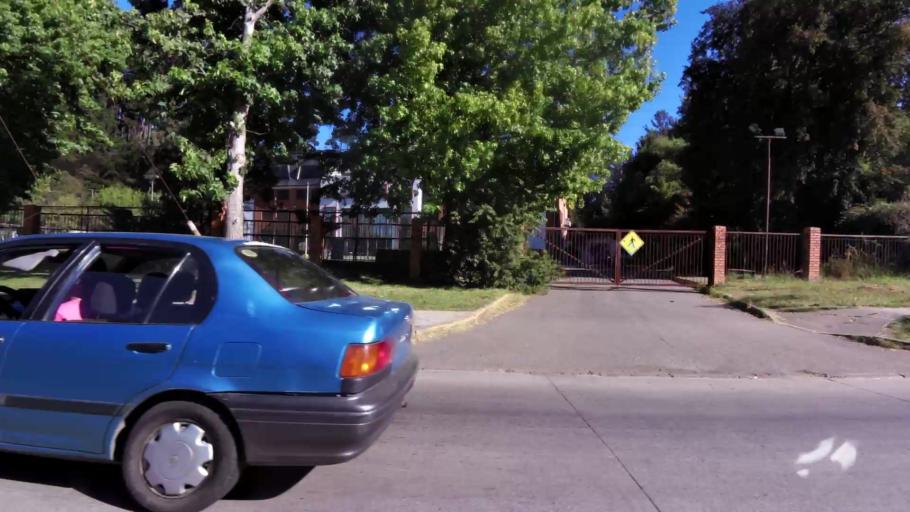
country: CL
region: Biobio
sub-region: Provincia de Concepcion
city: Concepcion
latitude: -36.8432
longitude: -73.1087
